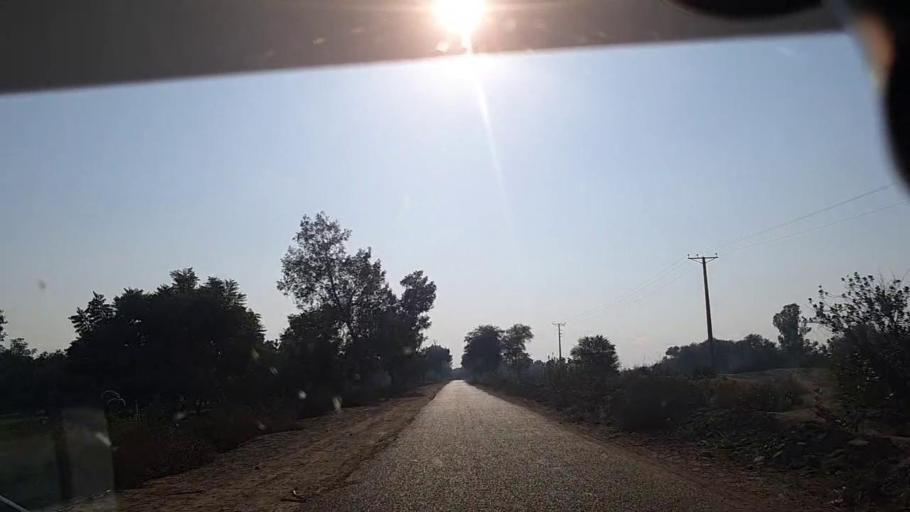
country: PK
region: Sindh
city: Sobhadero
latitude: 27.2378
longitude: 68.2805
